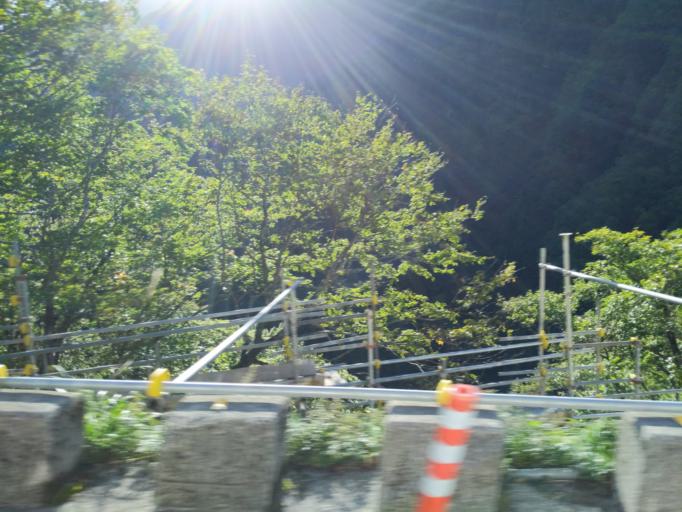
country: JP
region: Toyama
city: Kamiichi
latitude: 36.5083
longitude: 137.4484
